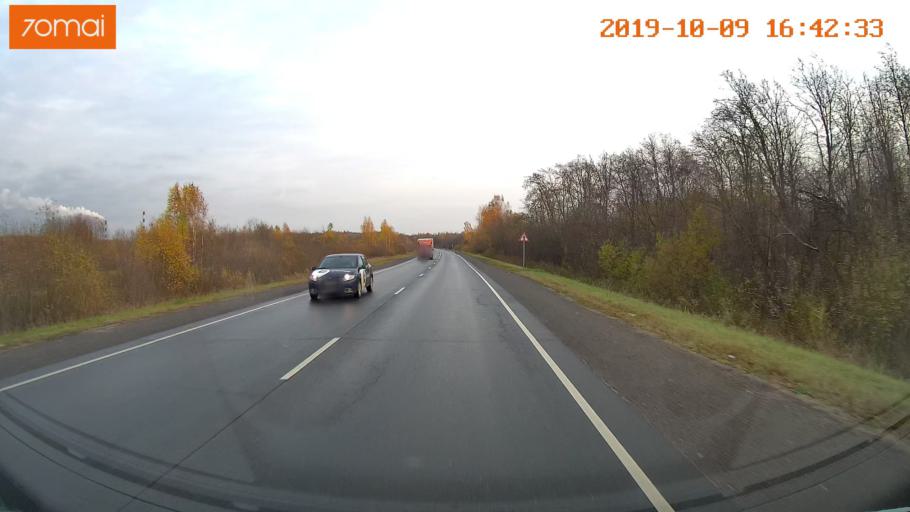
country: RU
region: Kostroma
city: Volgorechensk
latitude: 57.4610
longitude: 41.1021
